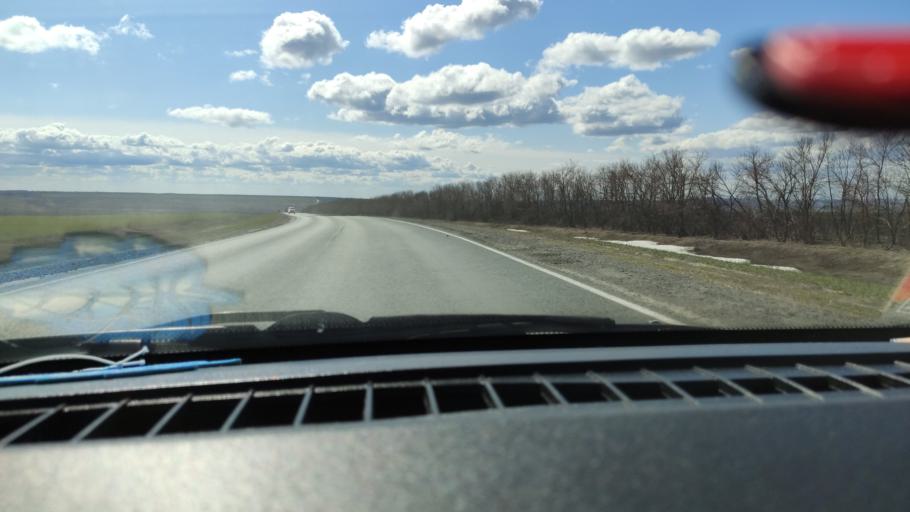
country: RU
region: Saratov
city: Dukhovnitskoye
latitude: 52.7607
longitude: 48.2416
